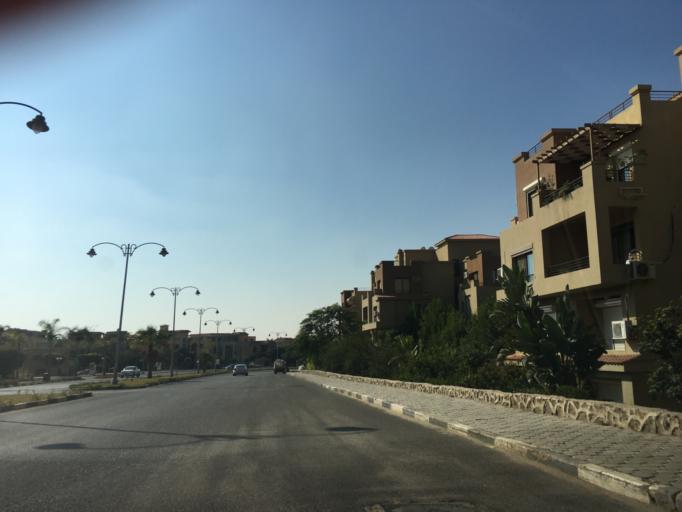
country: EG
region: Al Jizah
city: Awsim
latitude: 30.0661
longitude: 30.9502
